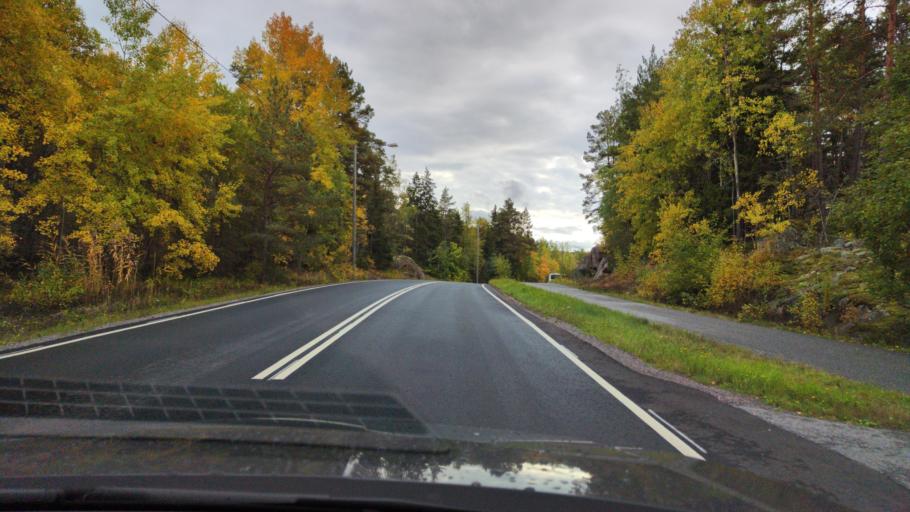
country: FI
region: Varsinais-Suomi
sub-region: Turku
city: Raisio
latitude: 60.3704
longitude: 22.1757
